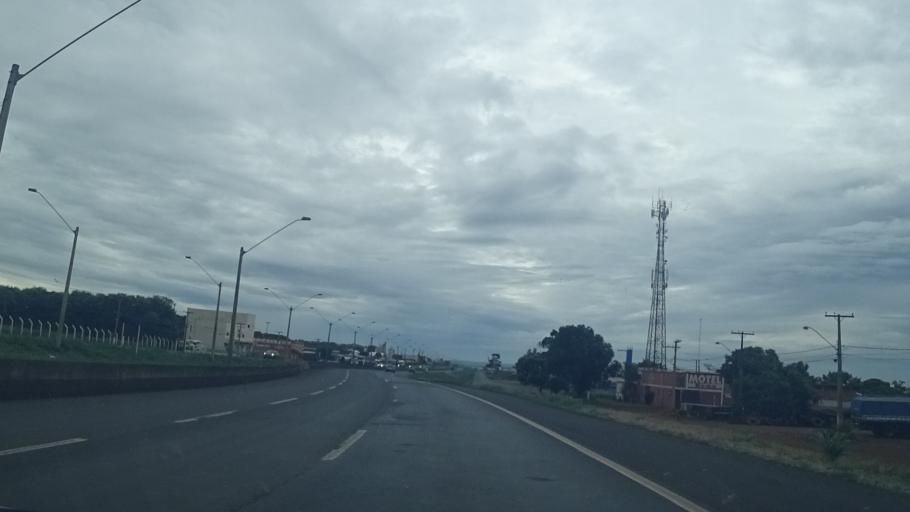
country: BR
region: Goias
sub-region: Itumbiara
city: Itumbiara
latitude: -18.3780
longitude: -49.2106
